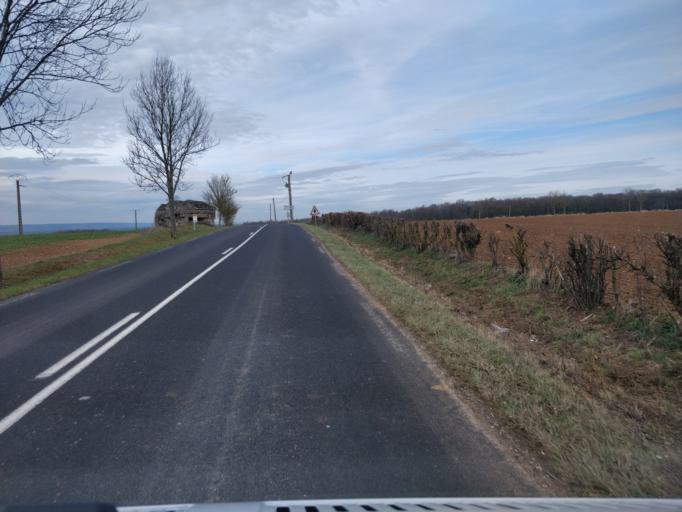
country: FR
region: Lorraine
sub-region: Departement de Meurthe-et-Moselle
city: Montauville
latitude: 48.9287
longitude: 5.9025
